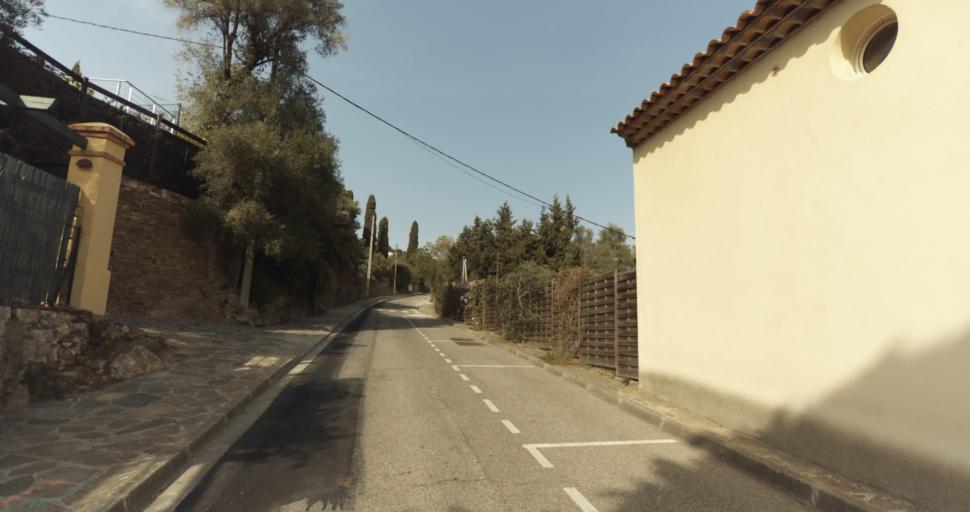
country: FR
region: Provence-Alpes-Cote d'Azur
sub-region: Departement du Var
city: Bormes-les-Mimosas
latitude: 43.1476
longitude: 6.3405
